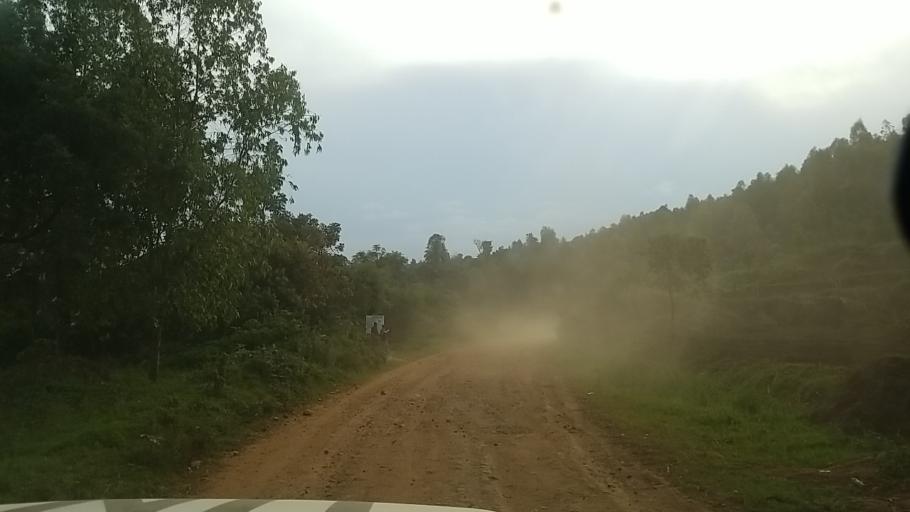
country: RW
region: Western Province
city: Cyangugu
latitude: -2.1051
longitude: 28.9094
